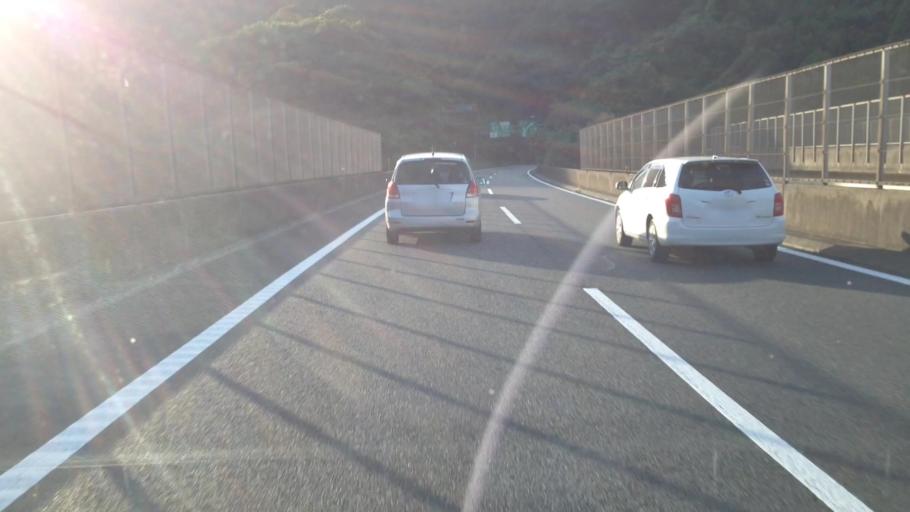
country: JP
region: Kanagawa
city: Yokosuka
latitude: 35.2832
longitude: 139.6254
